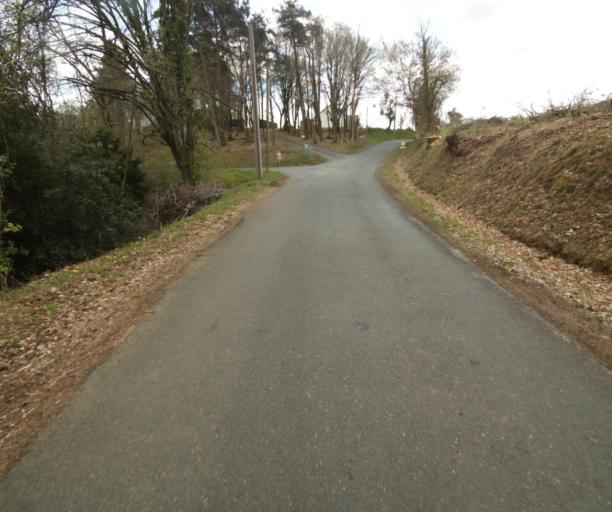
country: FR
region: Limousin
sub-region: Departement de la Correze
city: Sainte-Fortunade
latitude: 45.1977
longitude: 1.8564
